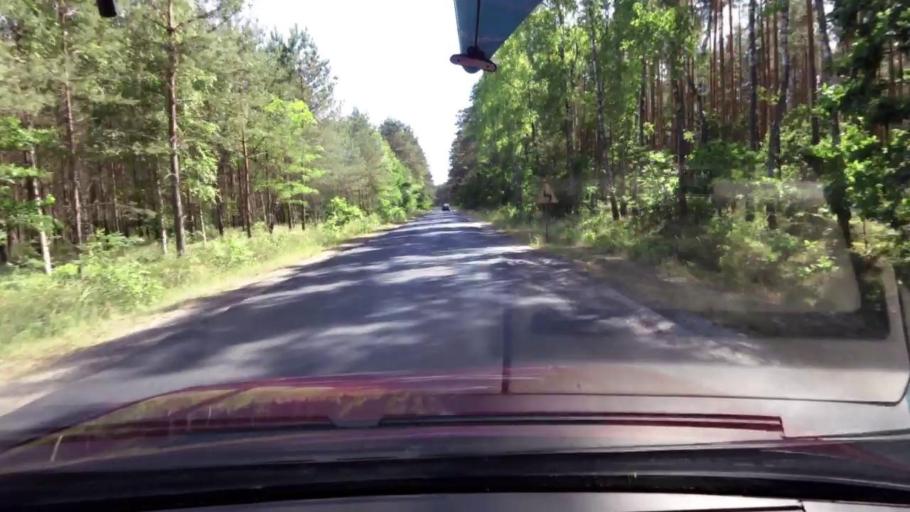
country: PL
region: Pomeranian Voivodeship
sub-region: Powiat slupski
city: Kepice
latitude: 54.3149
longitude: 16.9617
